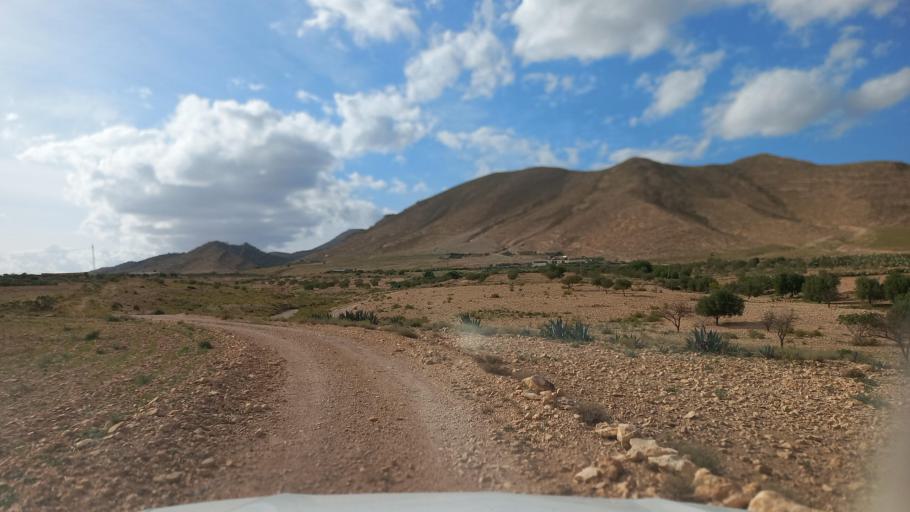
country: TN
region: Al Qasrayn
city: Sbiba
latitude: 35.4542
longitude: 9.0737
